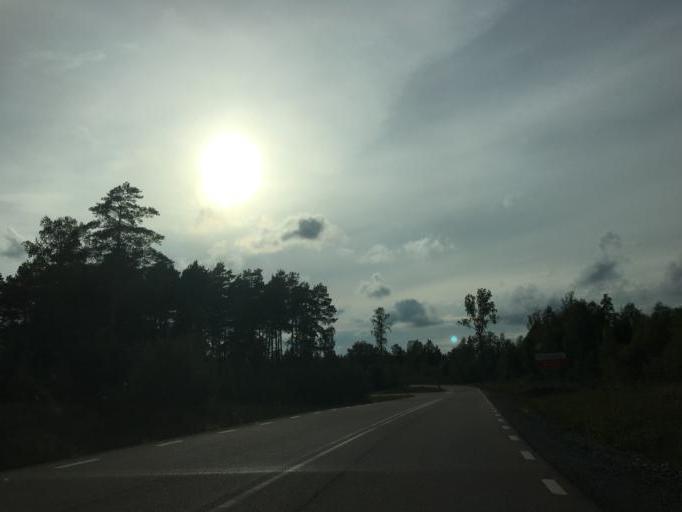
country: SE
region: Uppsala
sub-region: Enkopings Kommun
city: Hummelsta
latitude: 59.6393
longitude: 16.8777
